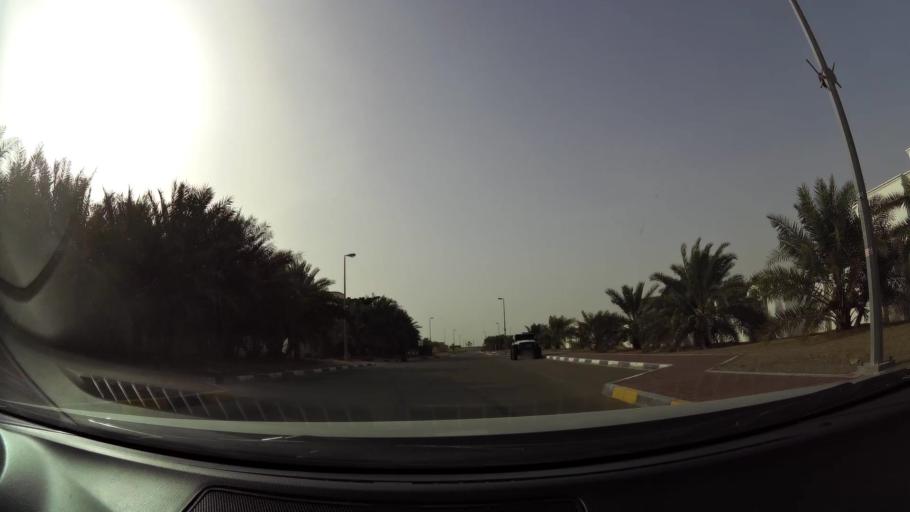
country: AE
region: Abu Dhabi
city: Al Ain
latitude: 24.2157
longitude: 55.6442
